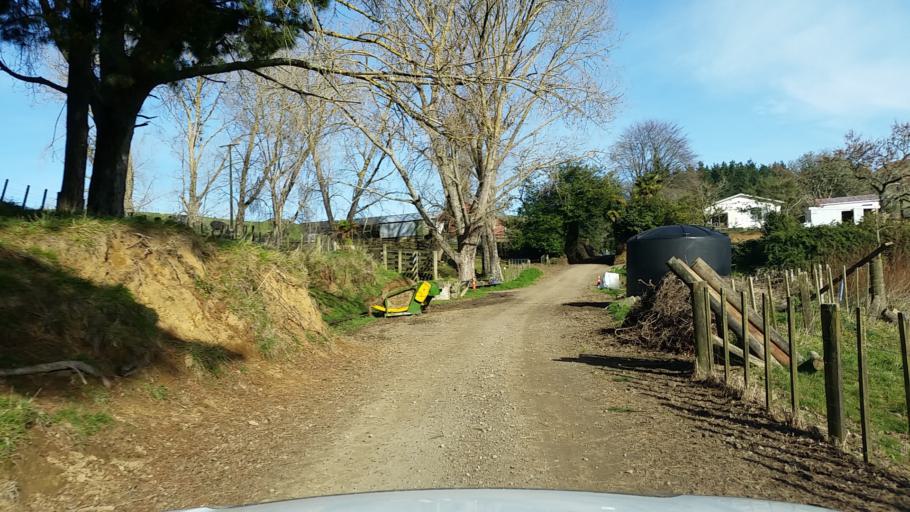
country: NZ
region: Taranaki
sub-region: South Taranaki District
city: Eltham
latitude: -39.3186
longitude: 174.5323
